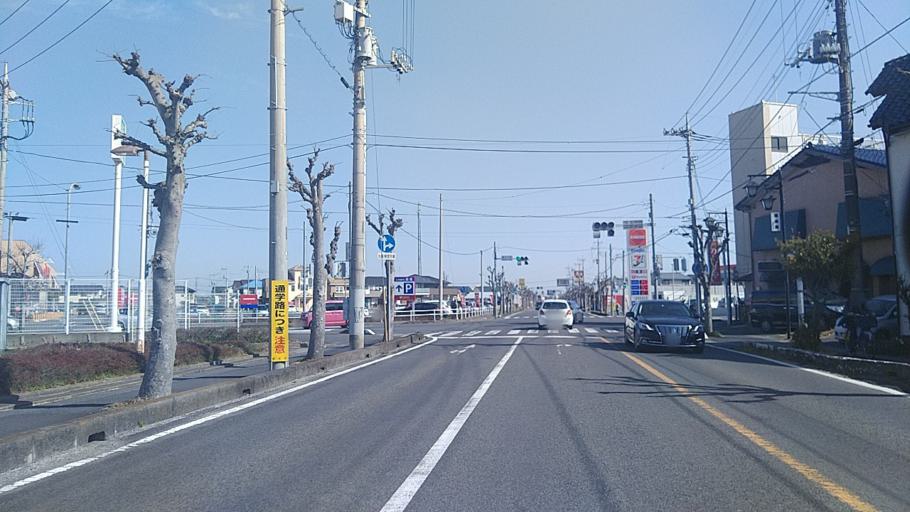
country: JP
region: Ibaraki
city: Toride
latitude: 35.8928
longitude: 140.0794
